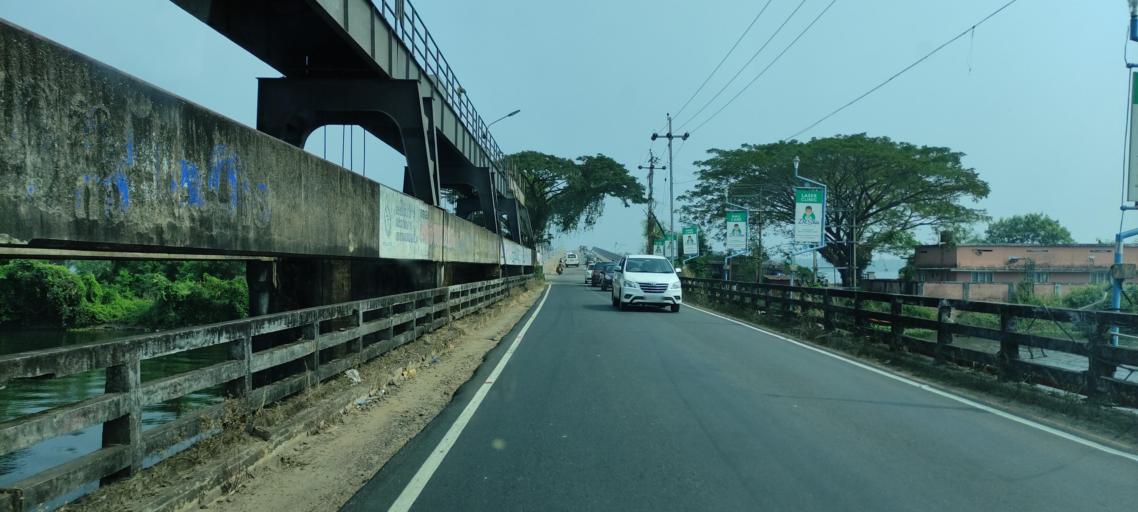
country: IN
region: Kerala
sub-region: Alappuzha
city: Shertallai
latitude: 9.6752
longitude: 76.3973
